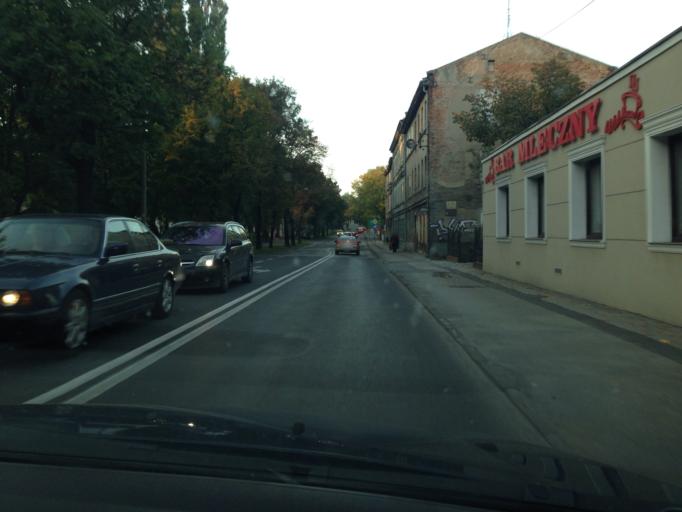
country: PL
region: Kujawsko-Pomorskie
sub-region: Powiat inowroclawski
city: Inowroclaw
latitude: 52.7965
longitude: 18.2648
